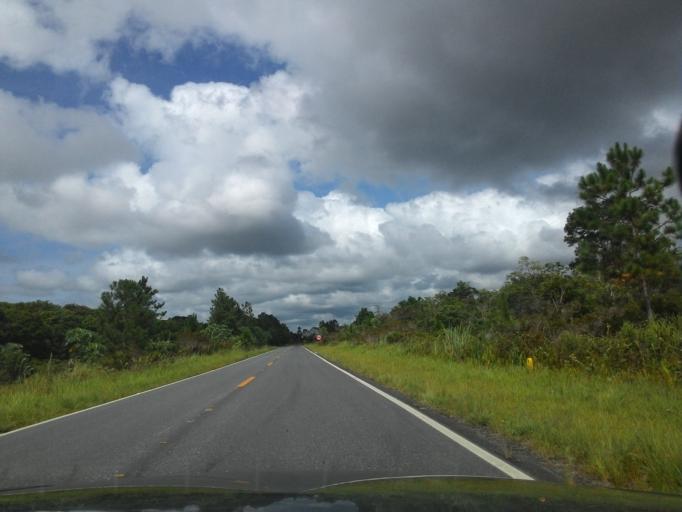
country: BR
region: Sao Paulo
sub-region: Iguape
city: Iguape
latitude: -24.8026
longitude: -47.6922
